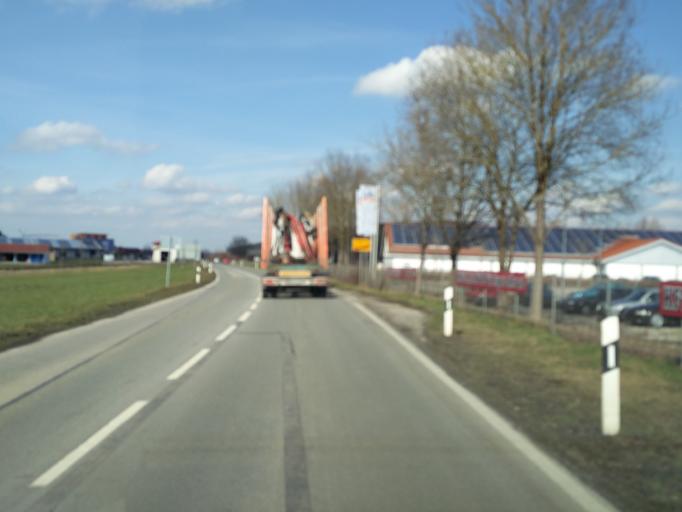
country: DE
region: Bavaria
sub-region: Upper Bavaria
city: Bad Endorf
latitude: 47.9179
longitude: 12.2926
